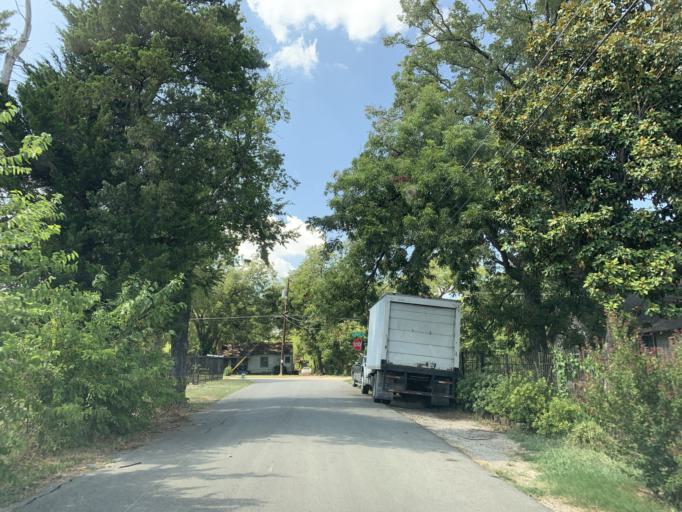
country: US
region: Texas
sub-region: Dallas County
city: Hutchins
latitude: 32.7094
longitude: -96.7672
